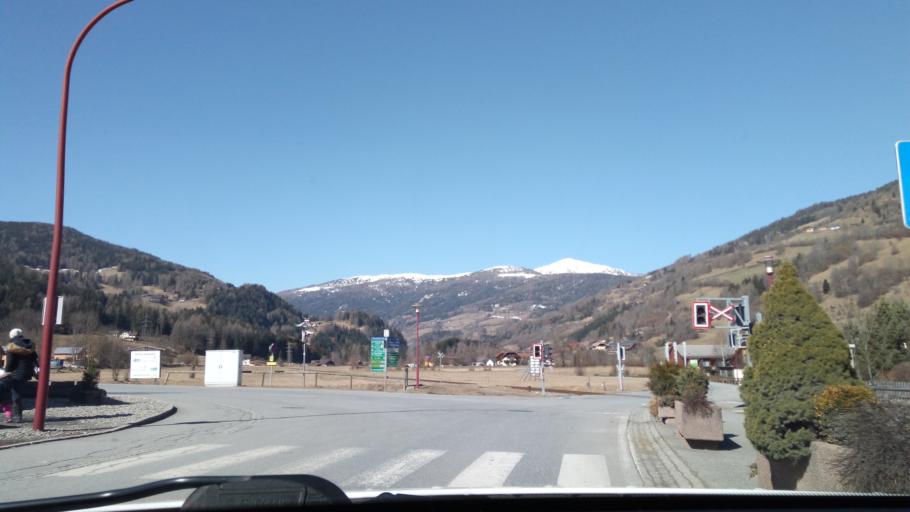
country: AT
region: Styria
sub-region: Politischer Bezirk Murau
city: Sankt Georgen ob Murau
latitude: 47.1019
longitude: 14.0878
